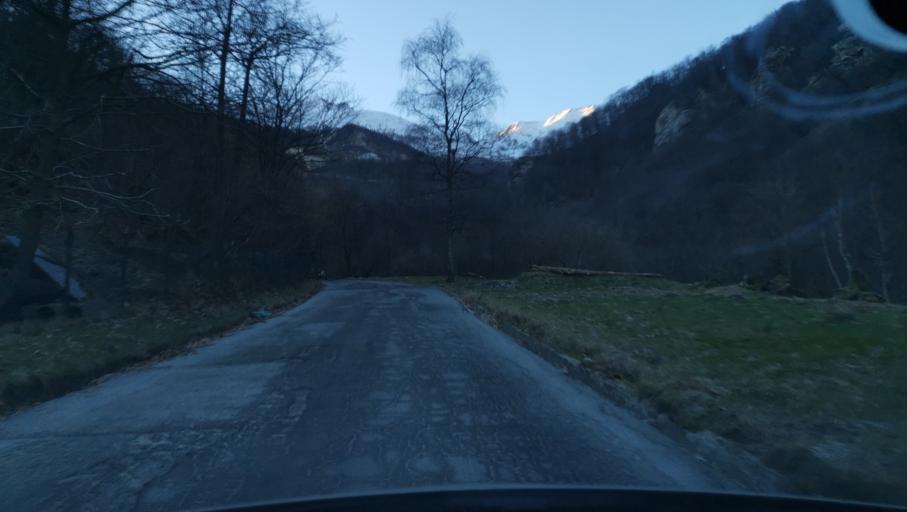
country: IT
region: Piedmont
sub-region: Provincia di Torino
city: Rora
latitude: 44.7730
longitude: 7.2053
